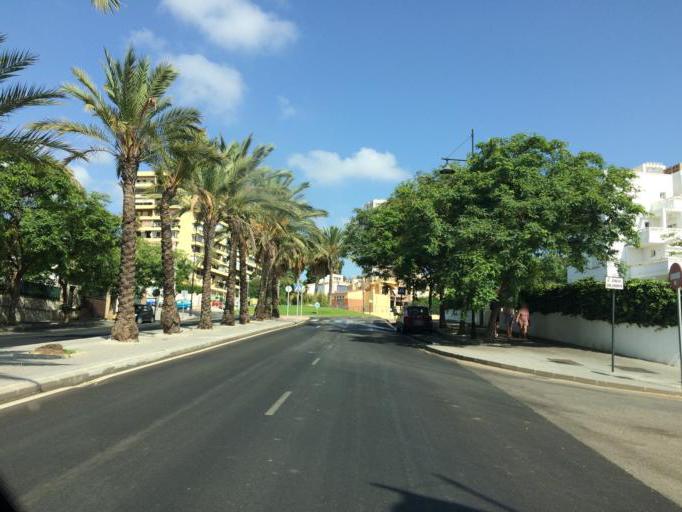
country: ES
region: Andalusia
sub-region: Provincia de Malaga
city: Torremolinos
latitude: 36.6377
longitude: -4.4918
